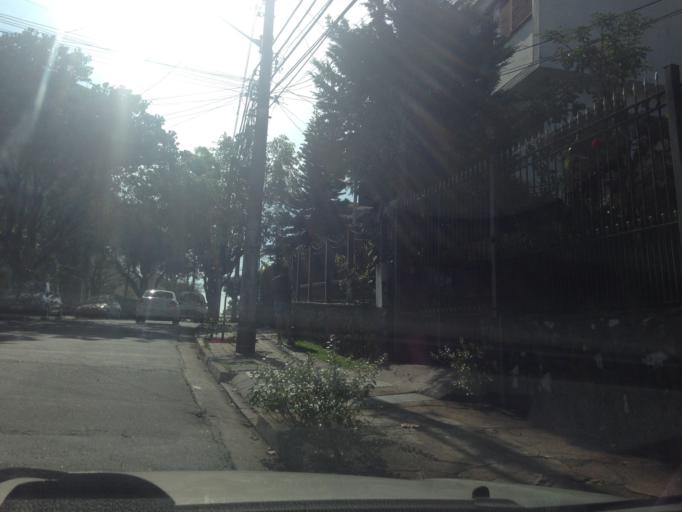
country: BR
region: Sao Paulo
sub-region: Sao Paulo
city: Sao Paulo
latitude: -23.5327
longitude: -46.7100
